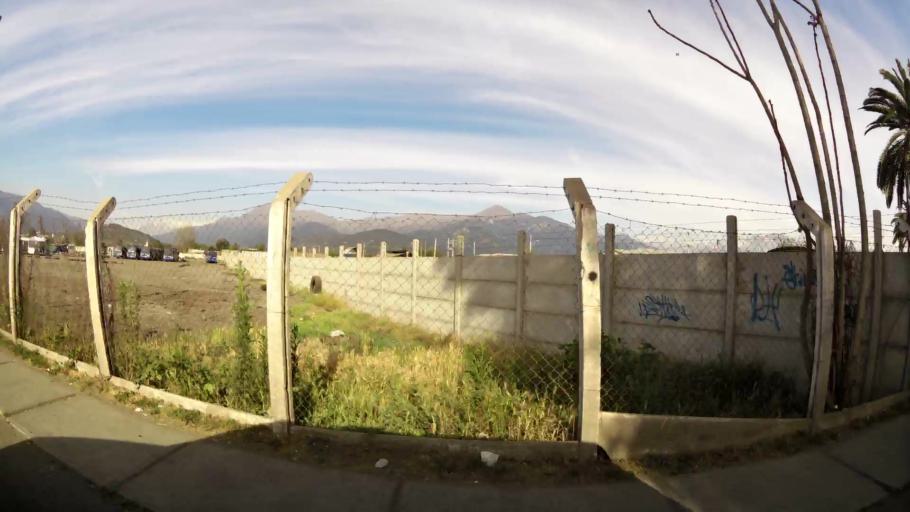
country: CL
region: Santiago Metropolitan
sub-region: Provincia de Cordillera
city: Puente Alto
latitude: -33.6142
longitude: -70.5747
